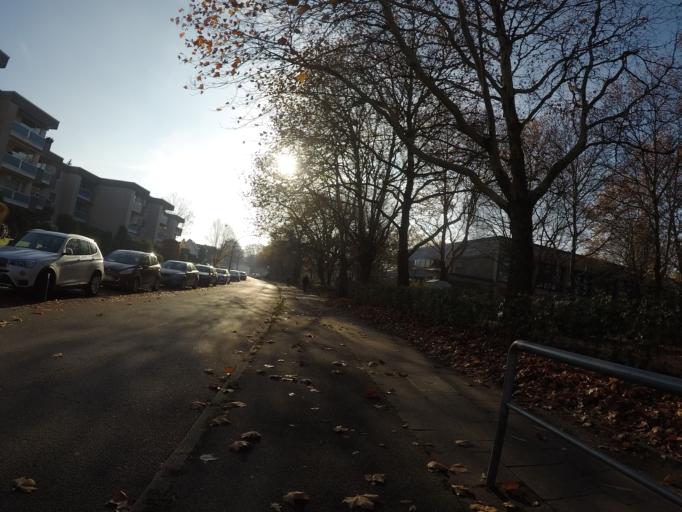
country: DE
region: Hamburg
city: Stellingen
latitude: 53.6024
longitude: 9.9244
